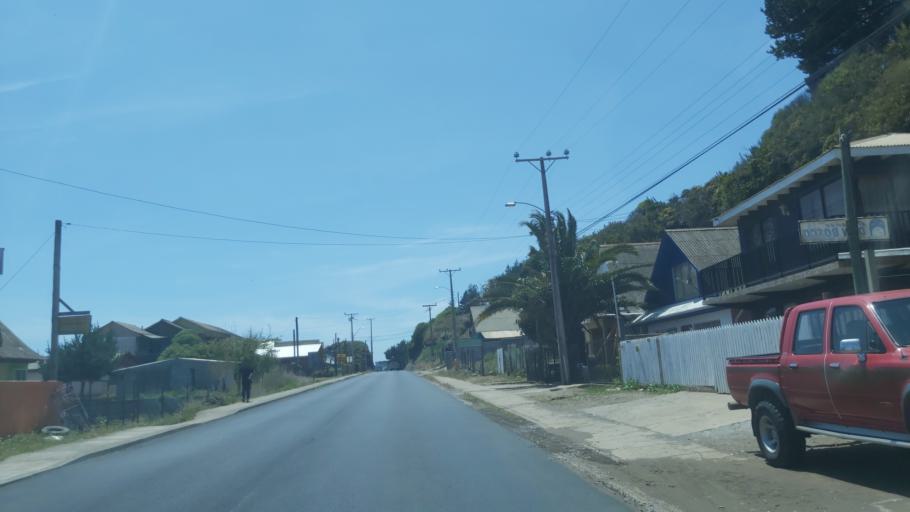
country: CL
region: Maule
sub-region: Provincia de Cauquenes
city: Cauquenes
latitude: -35.8398
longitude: -72.6278
